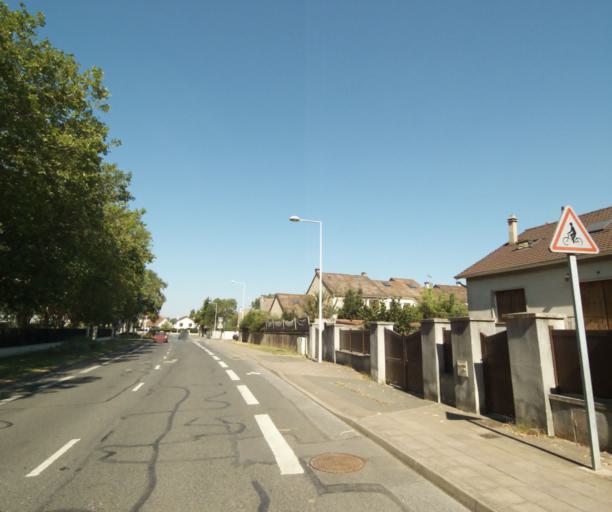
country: FR
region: Ile-de-France
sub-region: Departement de Seine-et-Marne
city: Moissy-Cramayel
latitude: 48.6244
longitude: 2.5972
